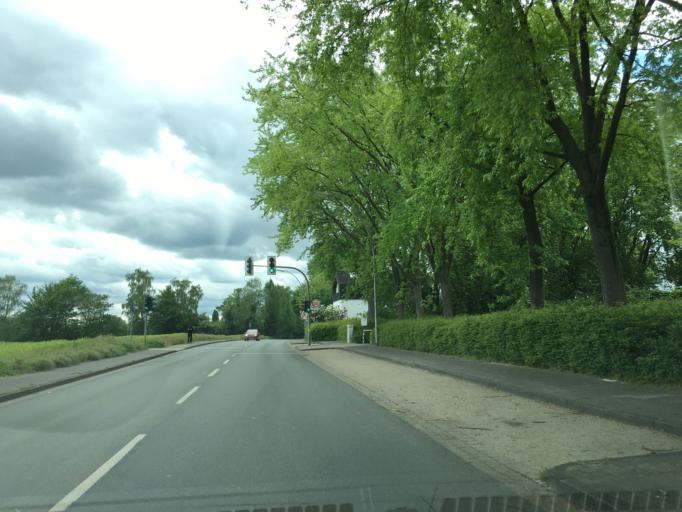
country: DE
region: North Rhine-Westphalia
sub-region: Regierungsbezirk Munster
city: Muenster
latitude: 51.9538
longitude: 7.5297
